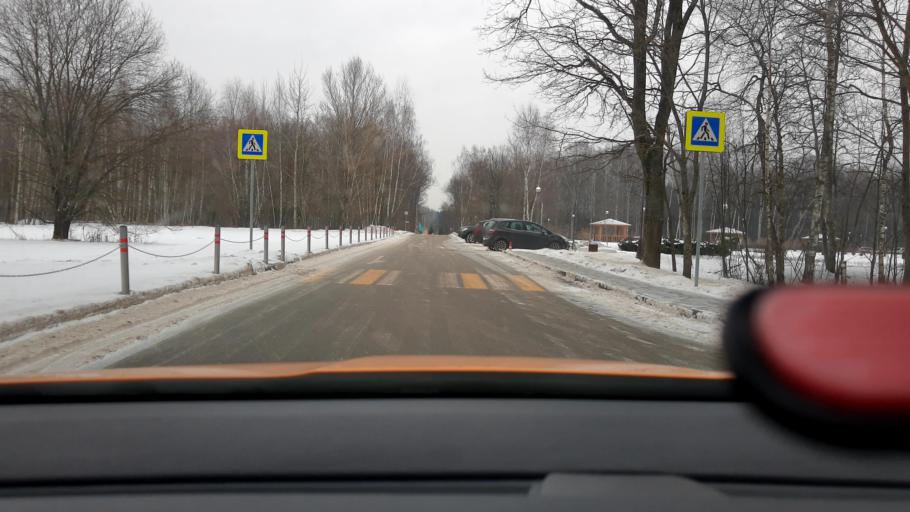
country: RU
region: Moskovskaya
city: Krasnogorsk
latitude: 55.8744
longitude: 37.3218
